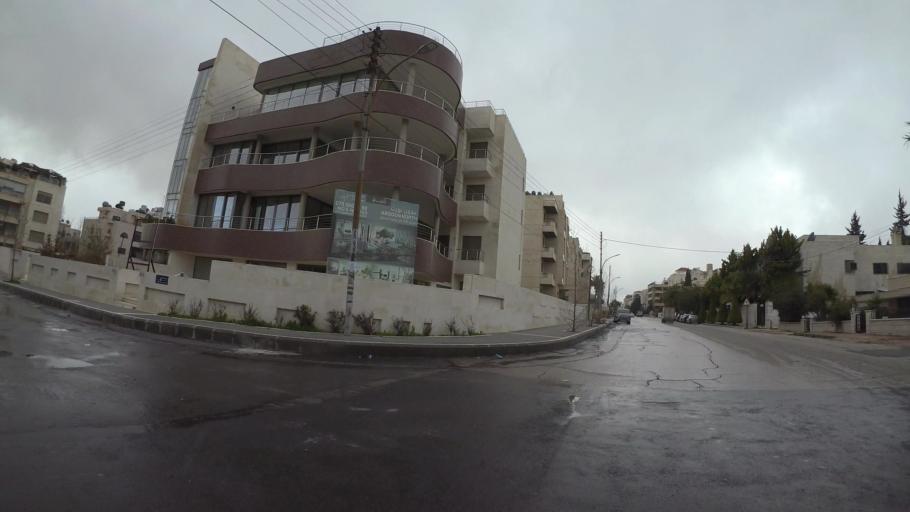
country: JO
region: Amman
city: Wadi as Sir
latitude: 31.9536
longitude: 35.8760
